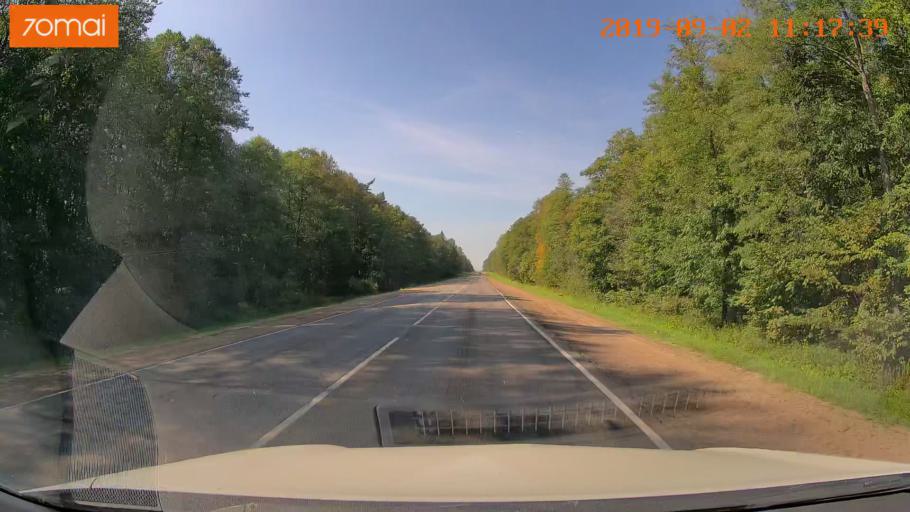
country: RU
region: Smolensk
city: Yekimovichi
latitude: 54.0602
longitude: 33.1136
